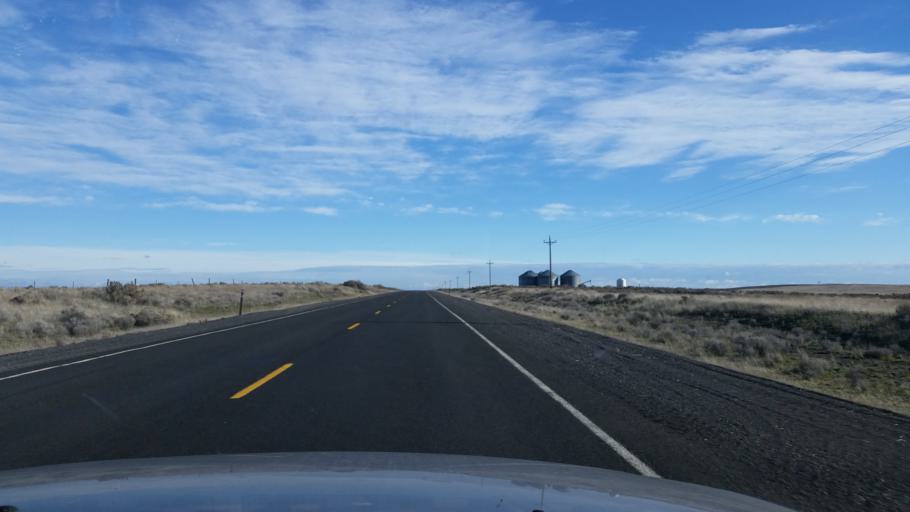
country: US
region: Washington
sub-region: Grant County
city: Warden
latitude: 47.3138
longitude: -118.7838
